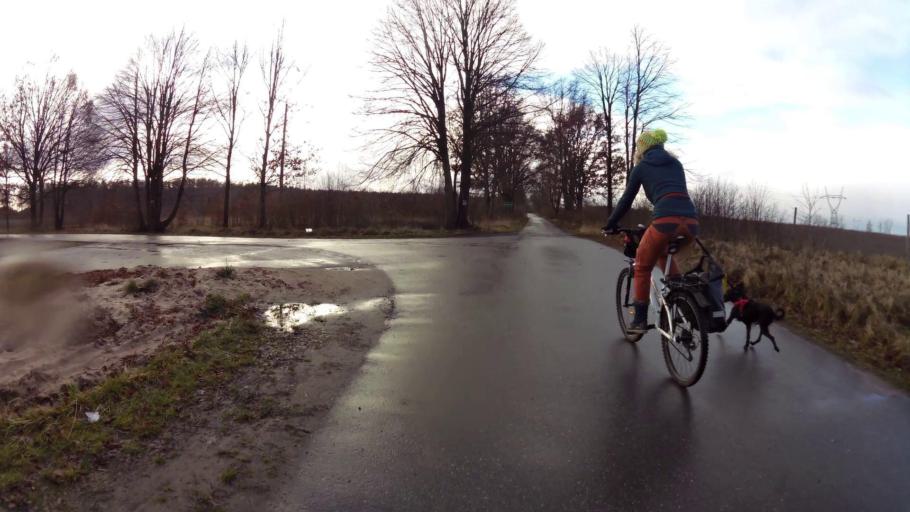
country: PL
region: West Pomeranian Voivodeship
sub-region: Powiat koszalinski
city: Sianow
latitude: 54.1241
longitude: 16.2974
